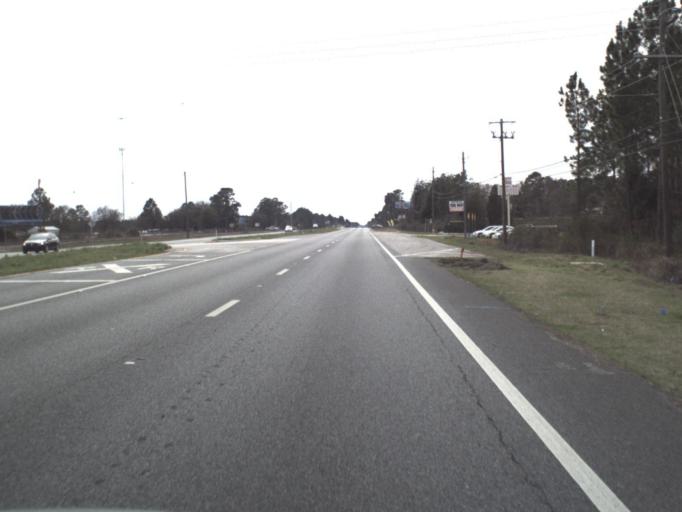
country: US
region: Florida
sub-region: Bay County
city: Youngstown
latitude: 30.2734
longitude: -85.5226
